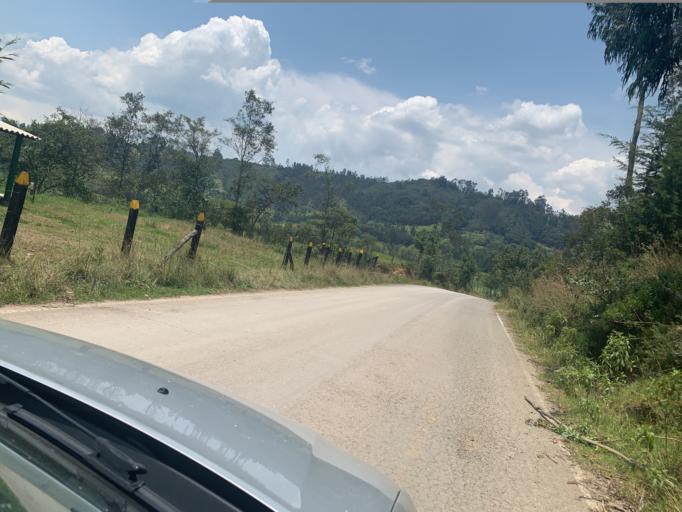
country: CO
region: Boyaca
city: Chiquinquira
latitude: 5.5810
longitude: -73.7486
